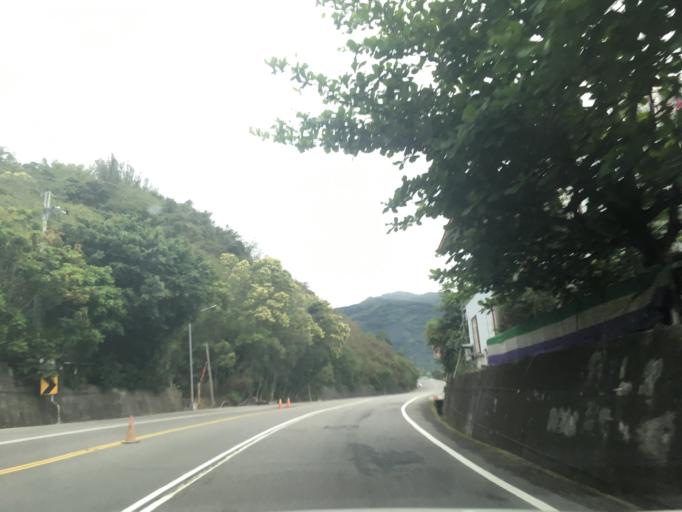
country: TW
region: Taiwan
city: Taitung City
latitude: 22.7496
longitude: 121.0546
